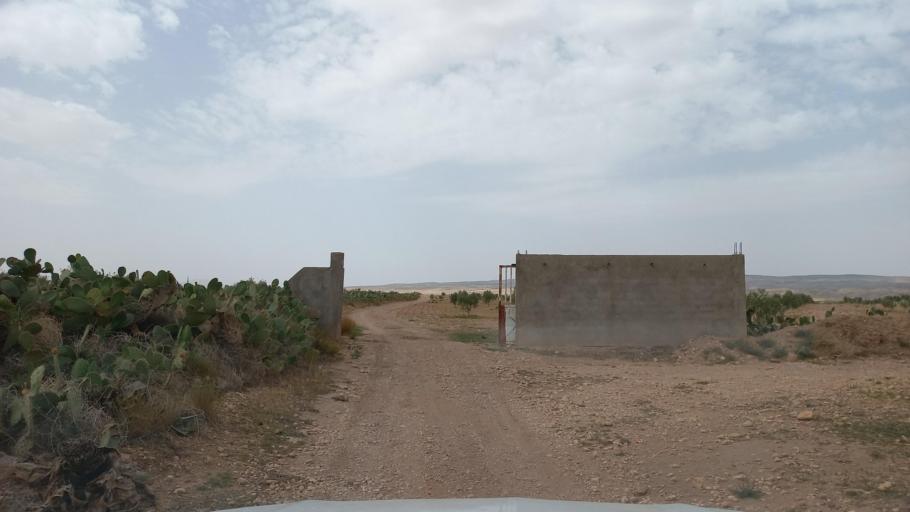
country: TN
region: Al Qasrayn
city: Kasserine
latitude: 35.2920
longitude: 9.0042
